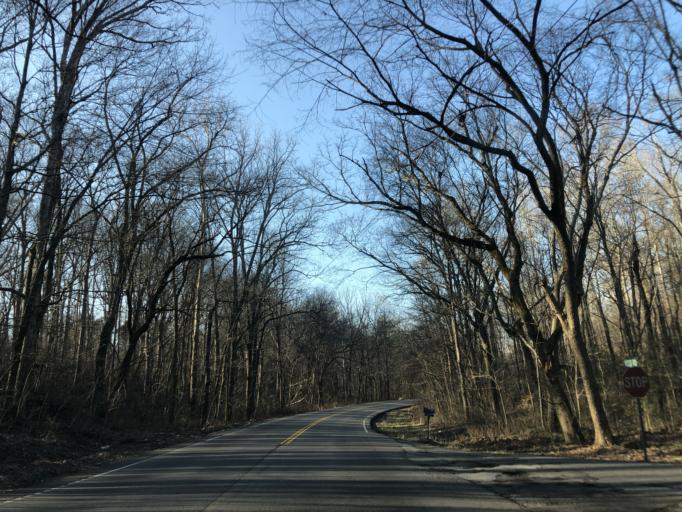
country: US
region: Tennessee
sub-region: Sumner County
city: White House
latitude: 36.5107
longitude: -86.6126
